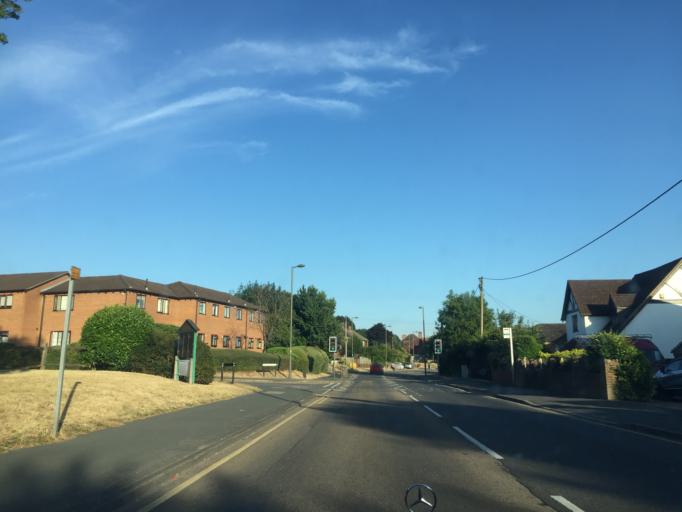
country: GB
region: England
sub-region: Surrey
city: Frimley
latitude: 51.3145
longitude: -0.7391
